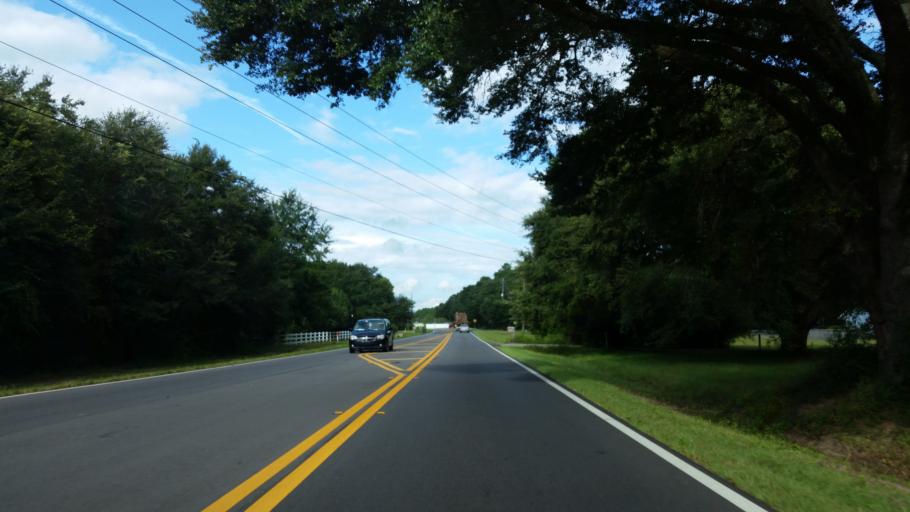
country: US
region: Florida
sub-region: Santa Rosa County
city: Wallace
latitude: 30.6474
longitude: -87.1612
